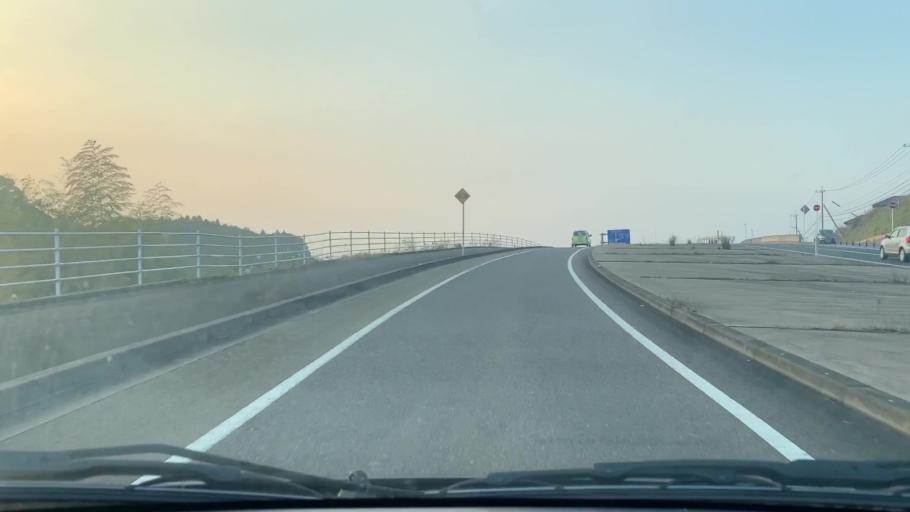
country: JP
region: Saga Prefecture
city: Imaricho-ko
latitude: 33.2630
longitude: 129.9097
